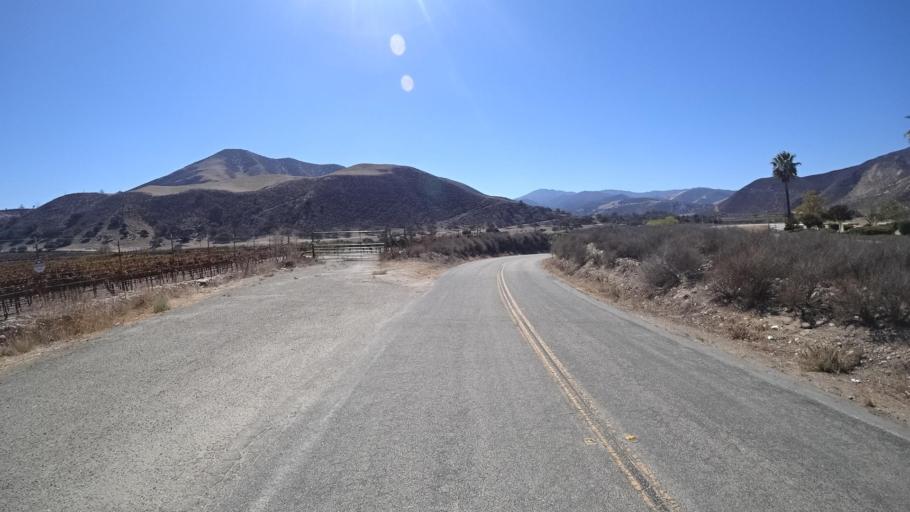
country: US
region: California
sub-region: Monterey County
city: Greenfield
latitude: 36.2824
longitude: -121.3203
